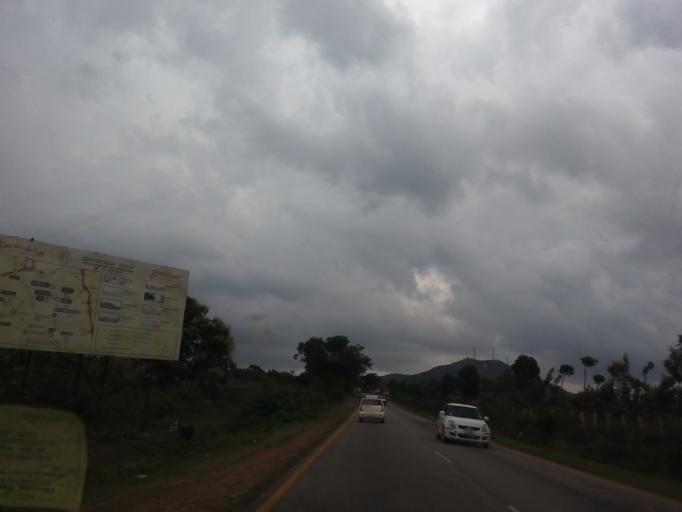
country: IN
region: Karnataka
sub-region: Hassan
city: Hassan
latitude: 13.0800
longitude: 76.0454
